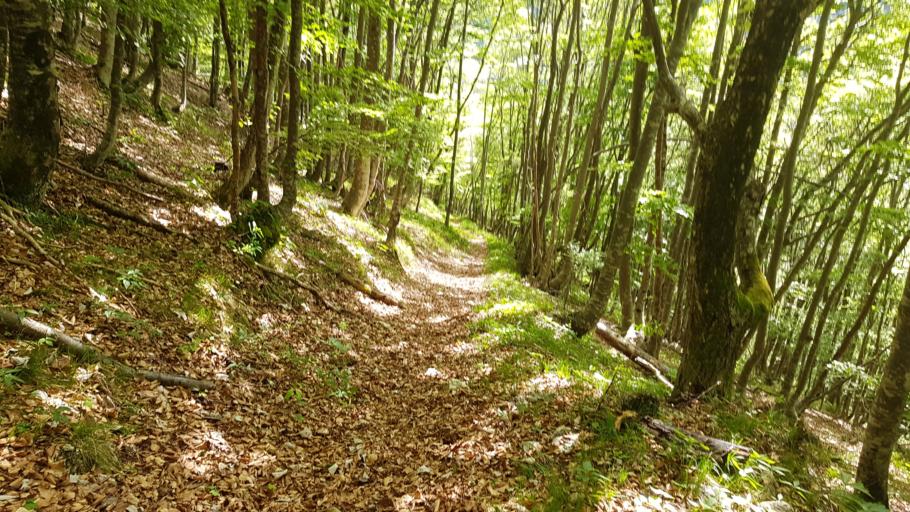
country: IT
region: Friuli Venezia Giulia
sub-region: Provincia di Udine
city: Moggio Udinese
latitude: 46.4844
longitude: 13.1996
